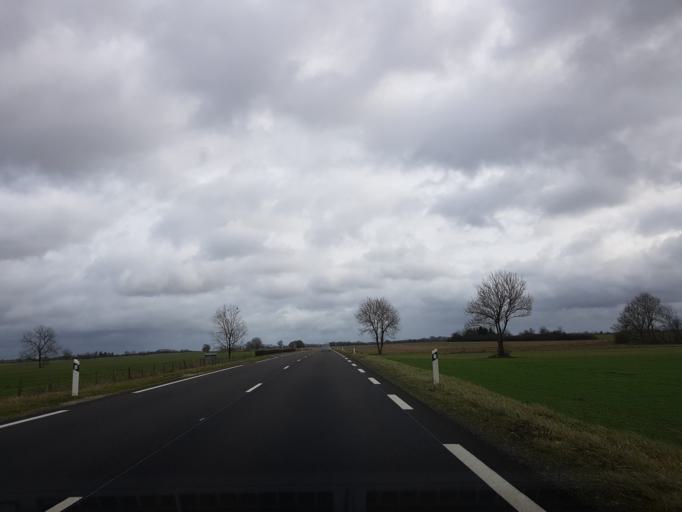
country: FR
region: Champagne-Ardenne
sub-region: Departement de la Haute-Marne
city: Chalindrey
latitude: 47.8476
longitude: 5.4289
